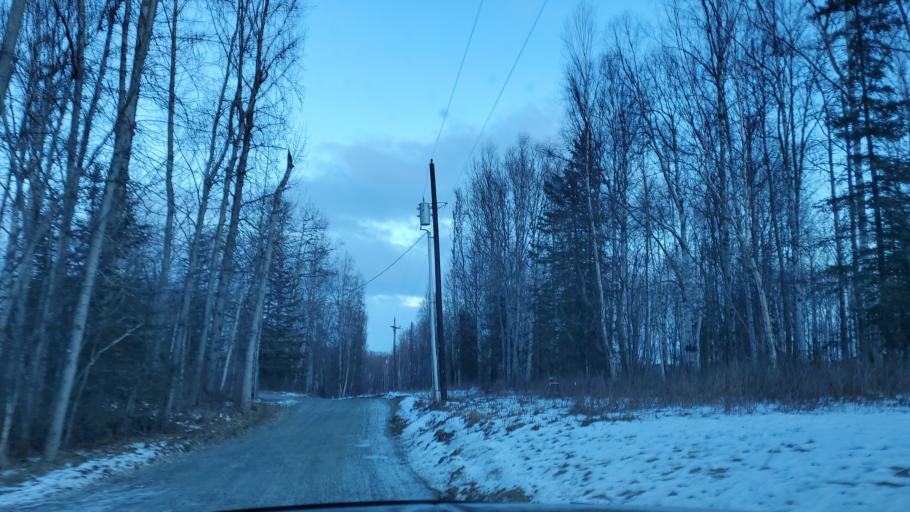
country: US
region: Alaska
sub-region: Matanuska-Susitna Borough
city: Lakes
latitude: 61.6635
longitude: -149.3259
